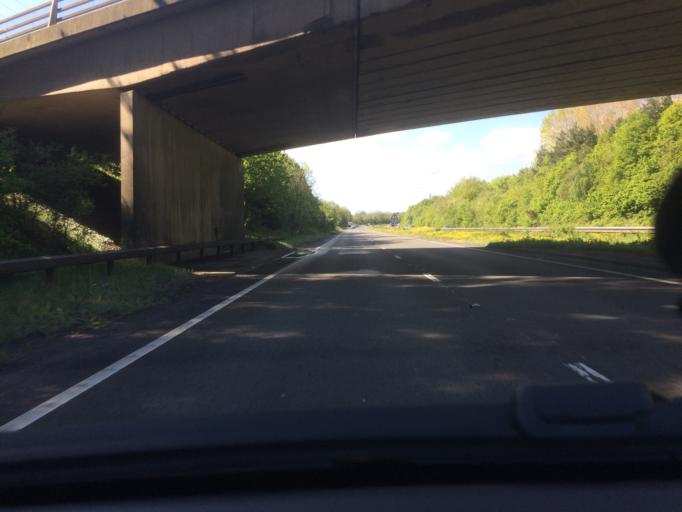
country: GB
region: England
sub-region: Cheshire West and Chester
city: Hoole
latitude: 53.1727
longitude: -2.8618
